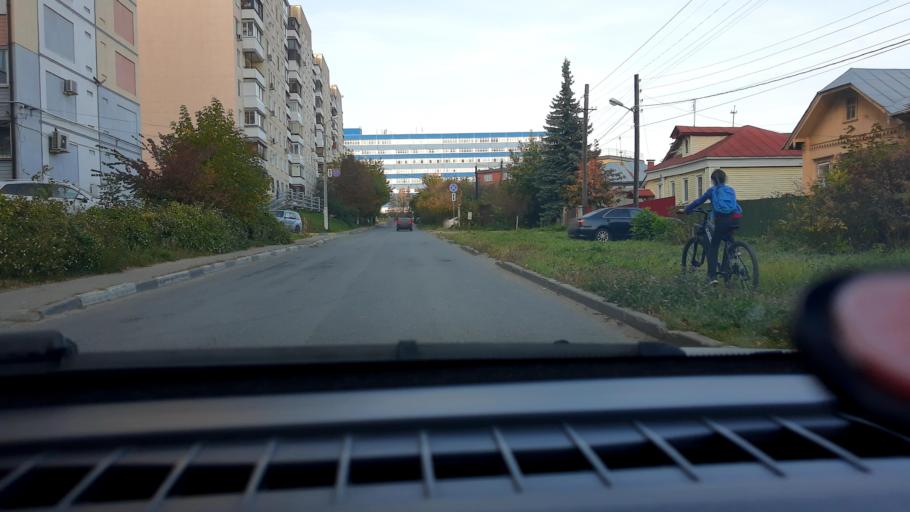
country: RU
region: Nizjnij Novgorod
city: Nizhniy Novgorod
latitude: 56.2788
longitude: 43.9950
